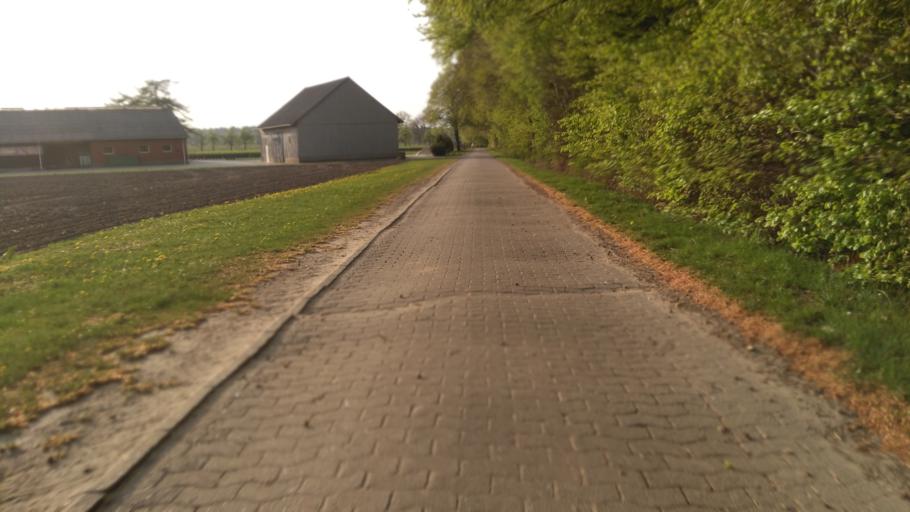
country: DE
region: Lower Saxony
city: Nottensdorf
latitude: 53.4680
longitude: 9.6361
